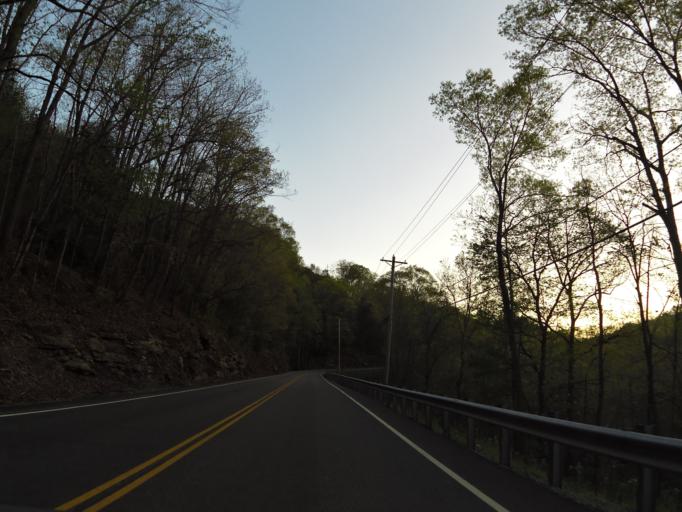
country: US
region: Tennessee
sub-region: Campbell County
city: Fincastle
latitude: 36.4175
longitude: -84.0917
